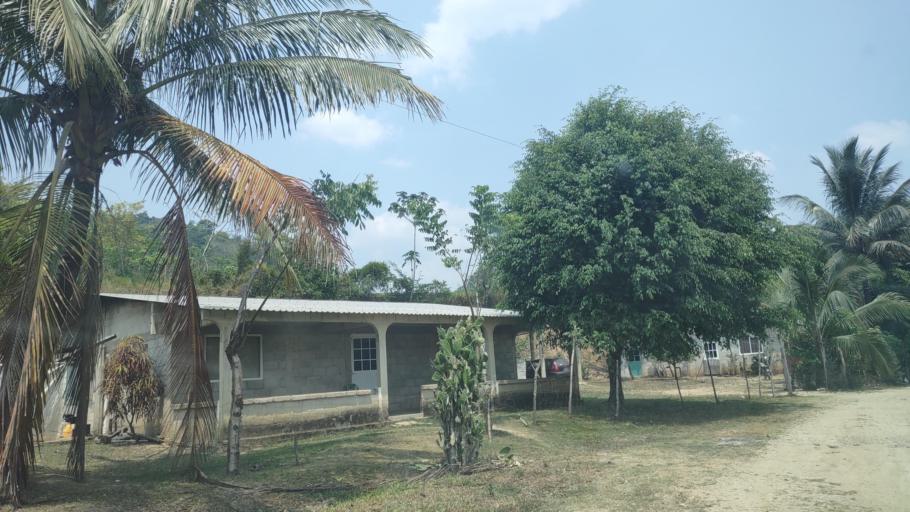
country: MX
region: Tabasco
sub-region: Huimanguillo
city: Francisco Rueda
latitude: 17.4954
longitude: -93.8444
